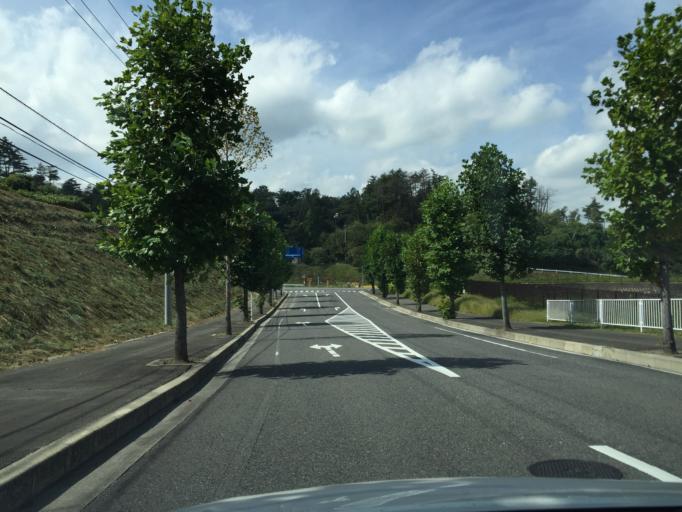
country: JP
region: Fukushima
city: Miharu
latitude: 37.4336
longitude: 140.5145
